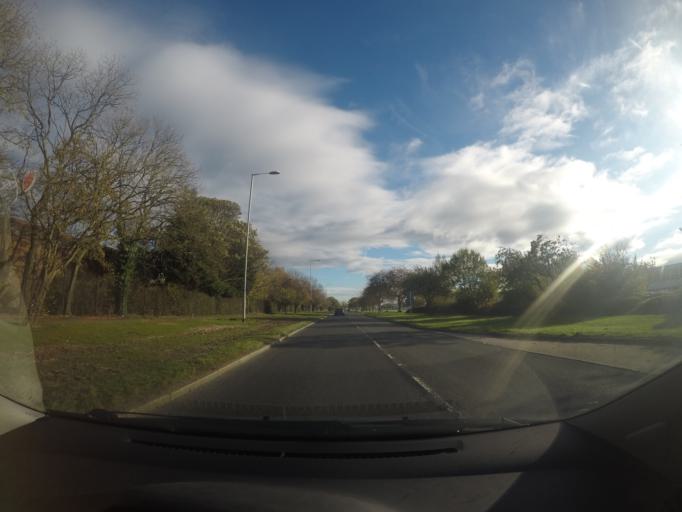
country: GB
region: England
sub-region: City and Borough of Leeds
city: Shadwell
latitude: 53.8313
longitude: -1.4634
